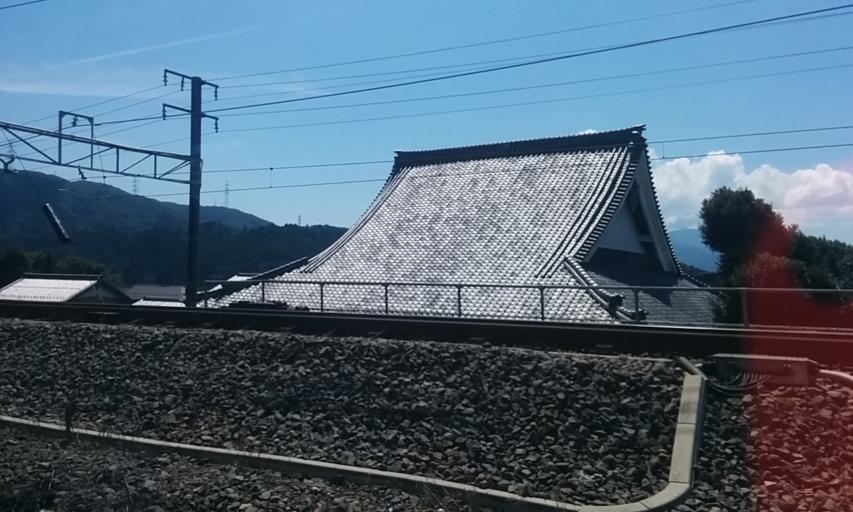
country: JP
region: Gifu
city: Tarui
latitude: 35.3644
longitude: 136.4754
